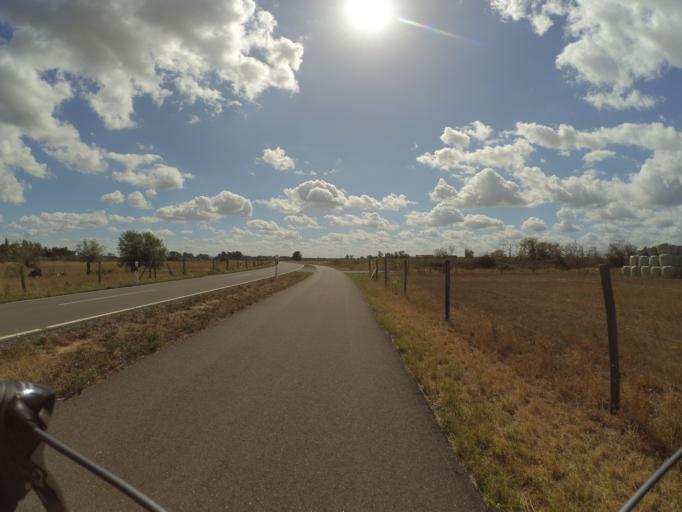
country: DE
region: North Rhine-Westphalia
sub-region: Regierungsbezirk Koln
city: Inden
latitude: 50.8901
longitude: 6.3754
